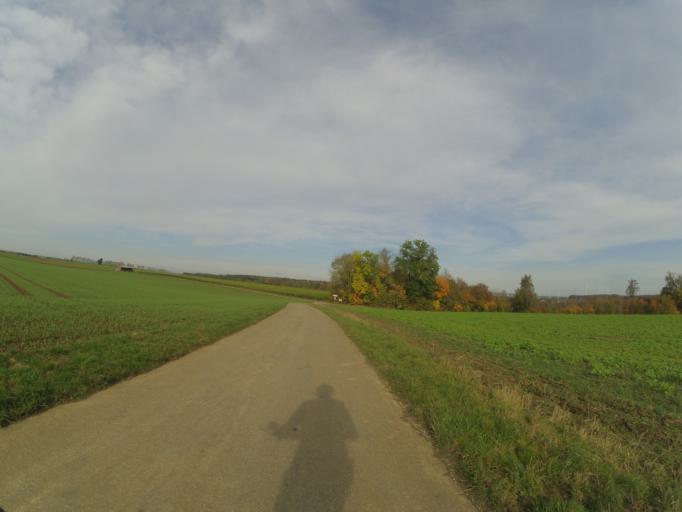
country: DE
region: Baden-Wuerttemberg
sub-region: Tuebingen Region
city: Blaubeuren
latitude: 48.4389
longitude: 9.8629
